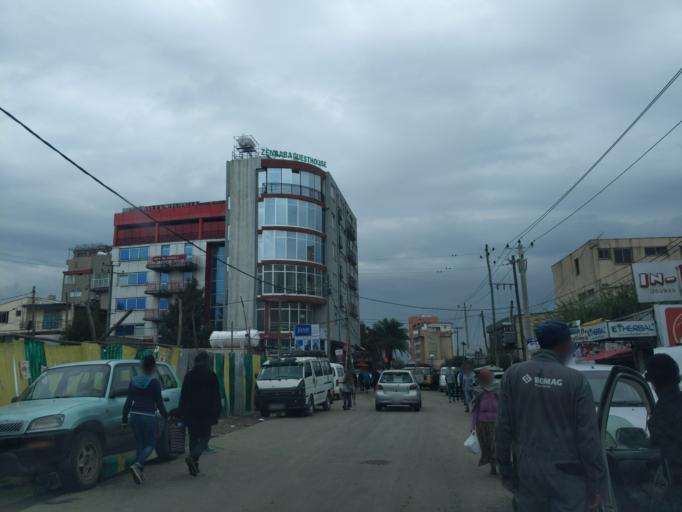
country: ET
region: Adis Abeba
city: Addis Ababa
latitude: 8.9894
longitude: 38.7923
